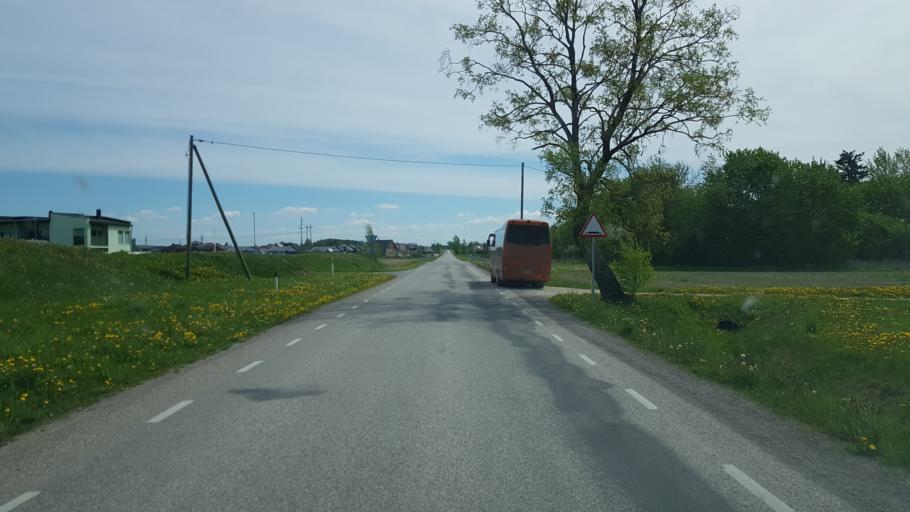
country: EE
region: Tartu
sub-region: Tartu linn
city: Tartu
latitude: 58.3583
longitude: 26.6427
